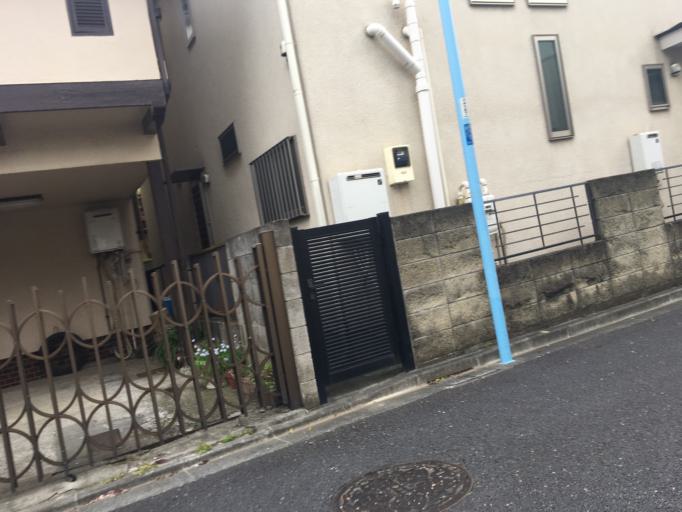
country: JP
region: Tokyo
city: Tokyo
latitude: 35.6953
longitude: 139.6359
